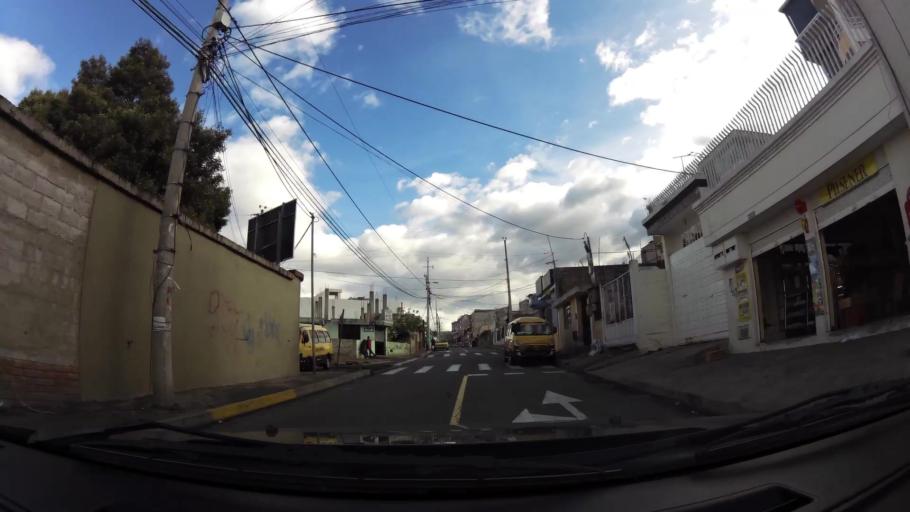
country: EC
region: Pichincha
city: Quito
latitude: -0.1348
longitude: -78.4566
